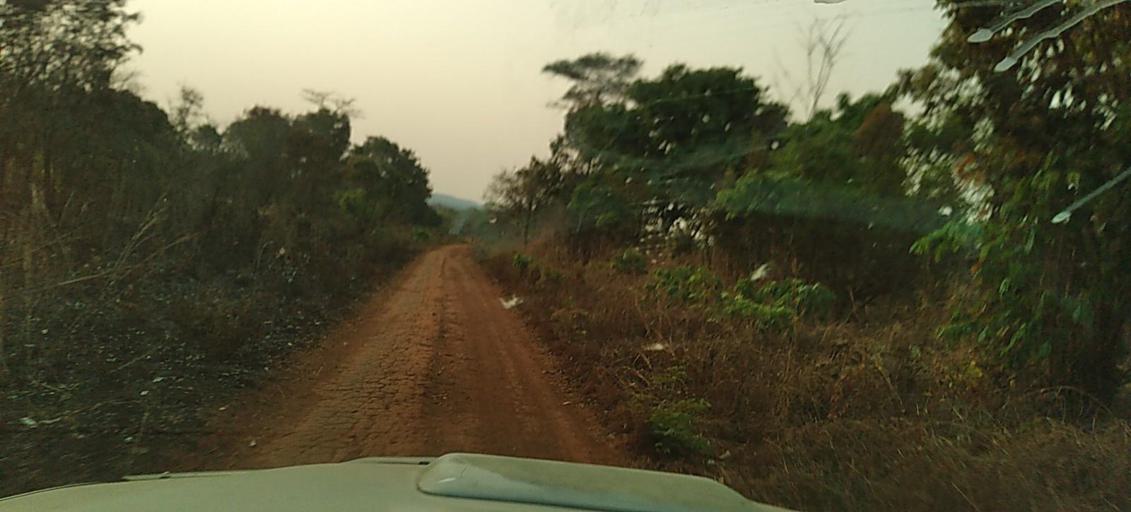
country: ZM
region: North-Western
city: Kasempa
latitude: -13.0745
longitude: 26.3865
